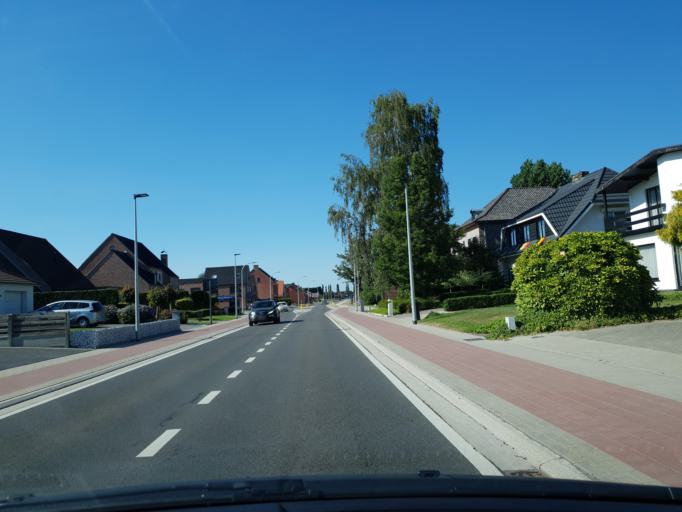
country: BE
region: Flanders
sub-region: Provincie Antwerpen
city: Beerse
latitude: 51.3288
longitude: 4.8555
